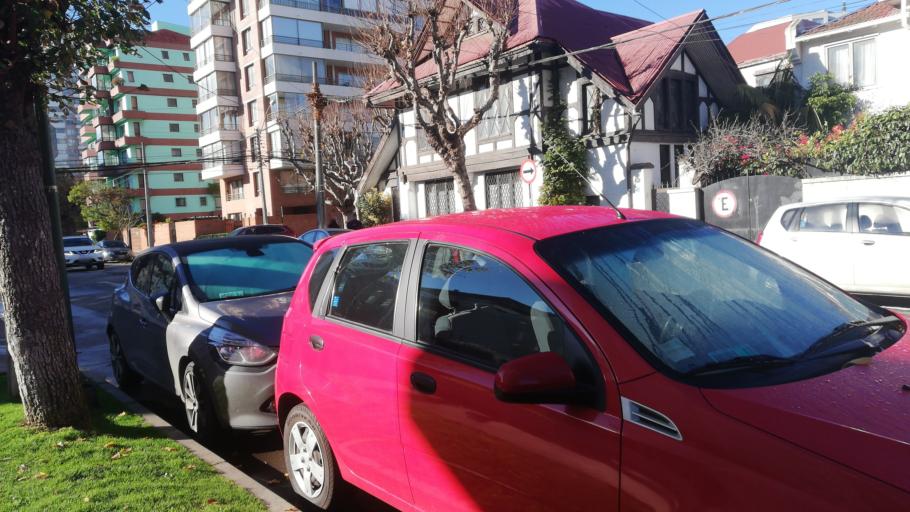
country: CL
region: Valparaiso
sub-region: Provincia de Valparaiso
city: Vina del Mar
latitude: -33.0187
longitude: -71.5485
